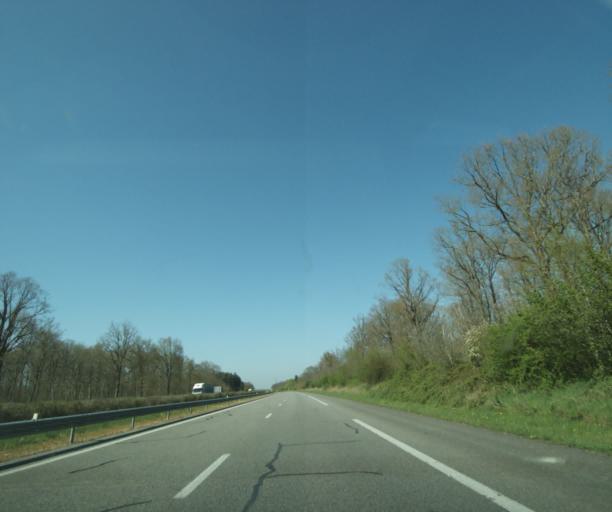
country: FR
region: Centre
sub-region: Departement du Loiret
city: Ouzouer-sur-Trezee
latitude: 47.7118
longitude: 2.7410
